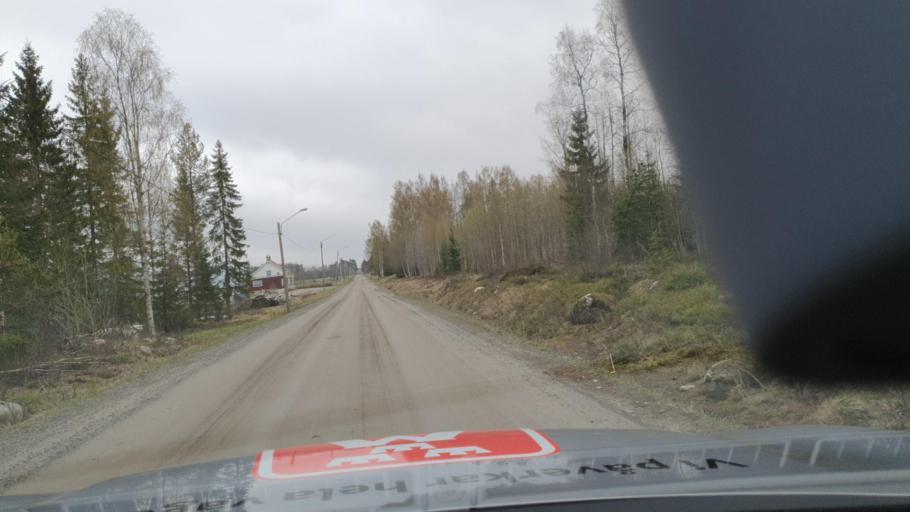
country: SE
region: Vaesterbotten
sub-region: Bjurholms Kommun
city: Bjurholm
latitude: 63.6548
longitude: 19.0384
